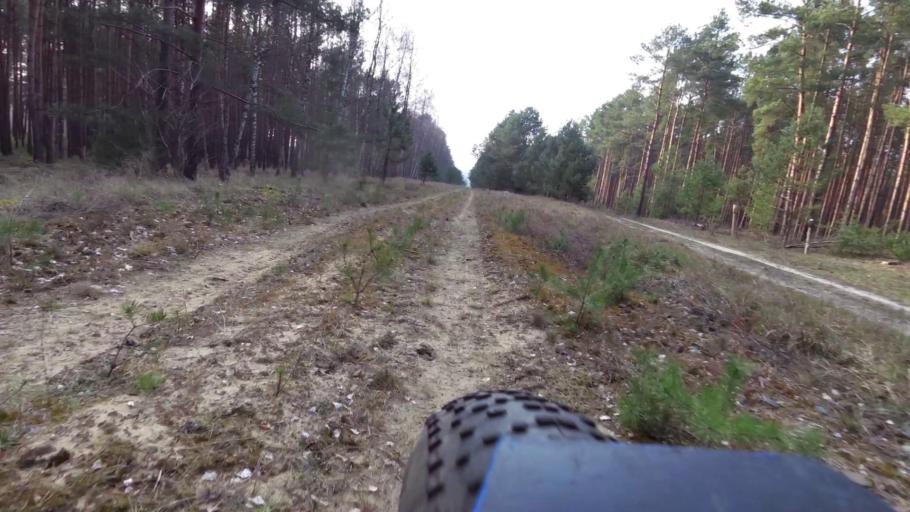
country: PL
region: Lubusz
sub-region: Powiat slubicki
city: Cybinka
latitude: 52.2500
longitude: 14.7462
